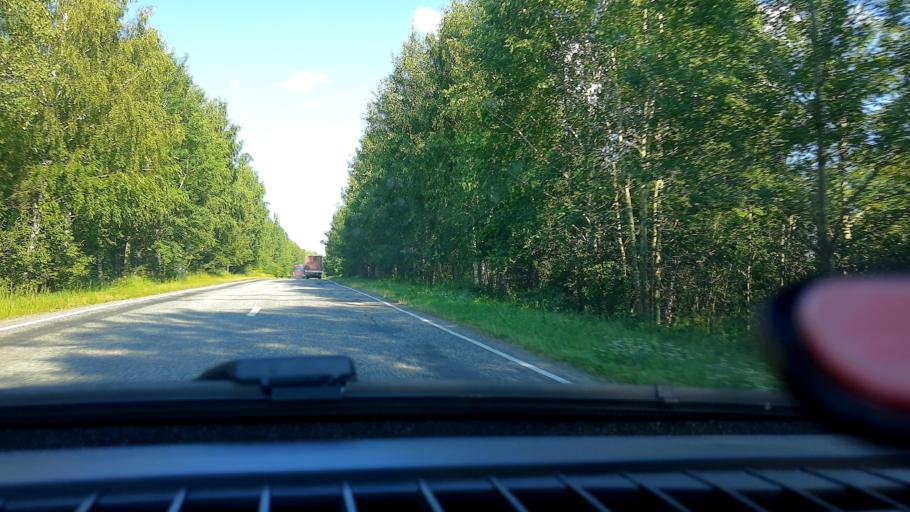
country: RU
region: Nizjnij Novgorod
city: Neklyudovo
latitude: 56.5170
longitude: 43.9216
